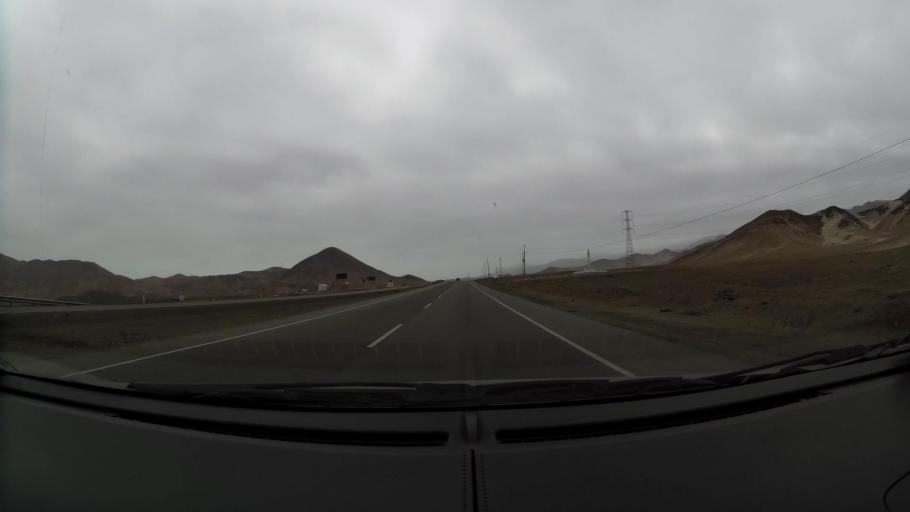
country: PE
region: Lima
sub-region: Barranca
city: Paramonga
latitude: -10.4594
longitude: -77.9185
